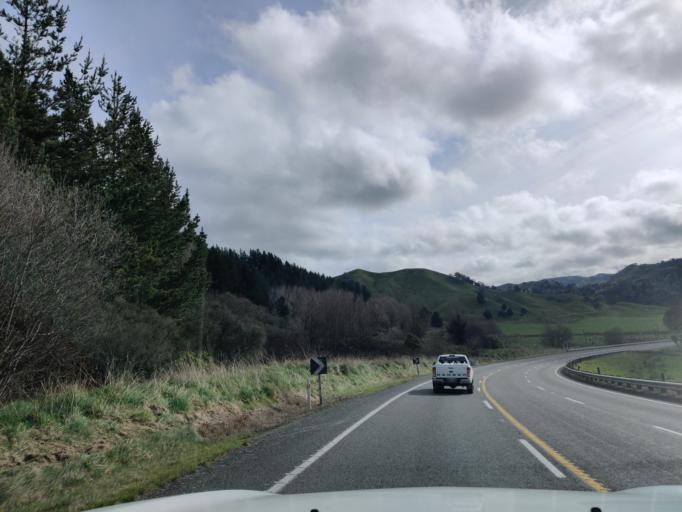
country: NZ
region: Manawatu-Wanganui
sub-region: Ruapehu District
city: Waiouru
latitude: -39.8239
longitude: 175.7764
